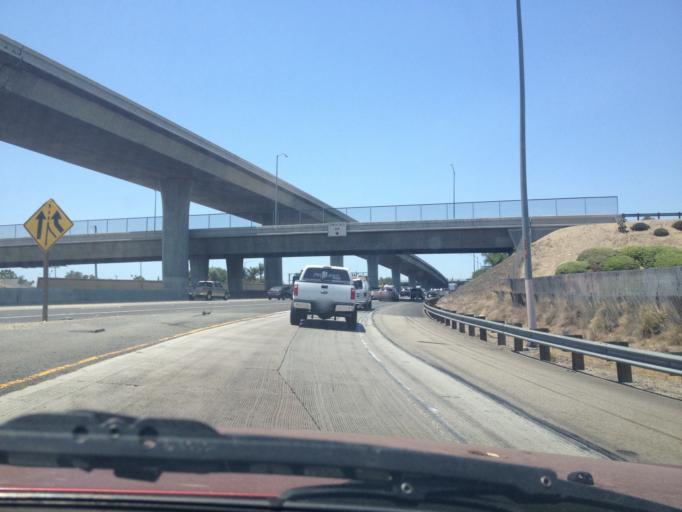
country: US
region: California
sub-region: Orange County
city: Placentia
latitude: 33.8513
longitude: -117.8782
